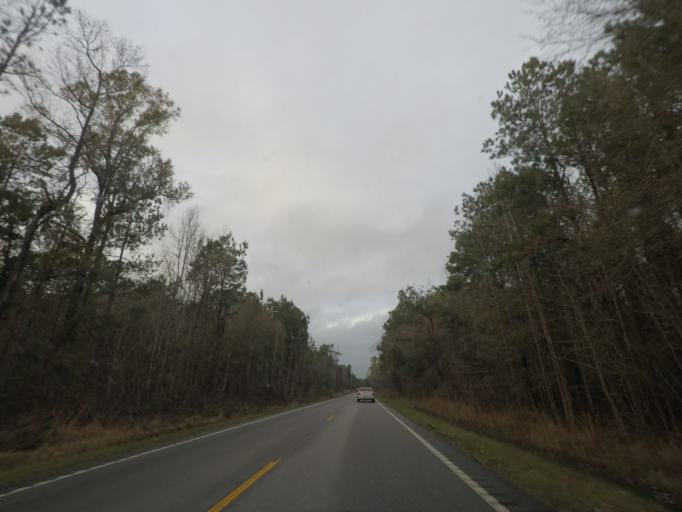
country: US
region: South Carolina
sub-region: Dorchester County
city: Saint George
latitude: 33.0430
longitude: -80.5956
